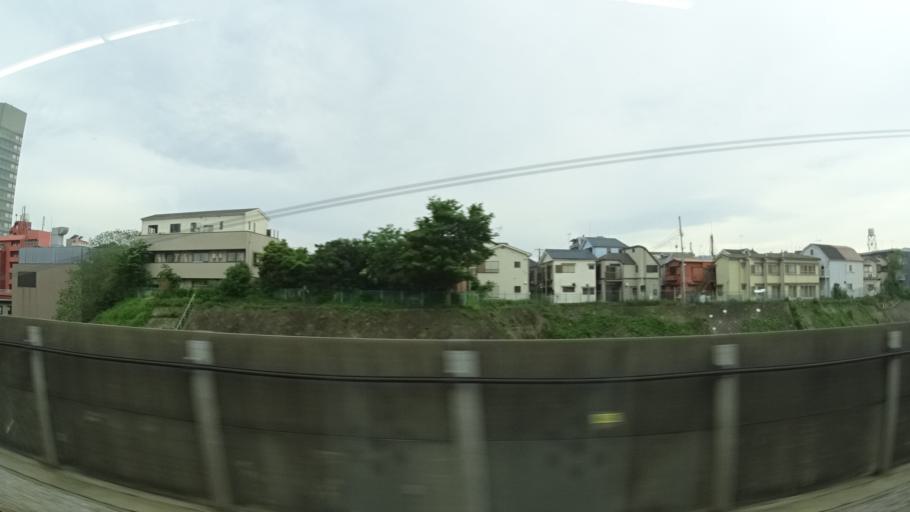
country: JP
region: Saitama
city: Kawaguchi
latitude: 35.7402
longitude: 139.7586
